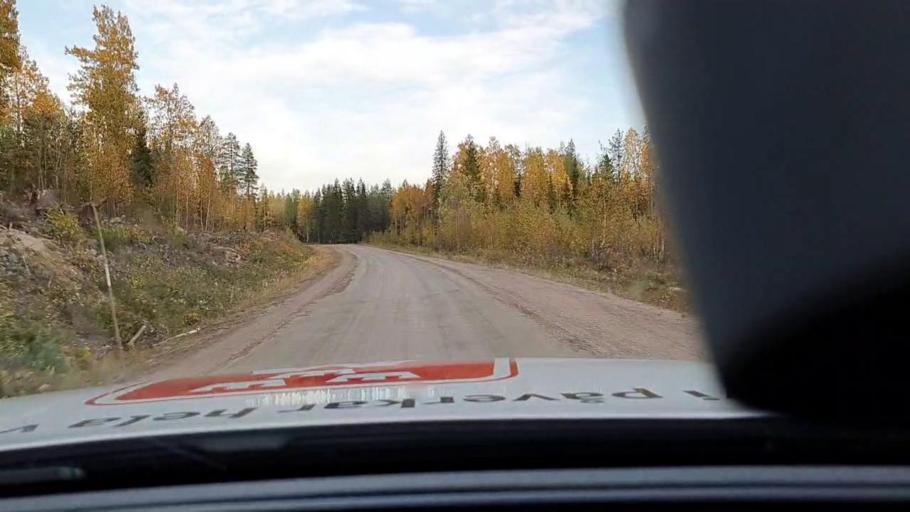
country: SE
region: Norrbotten
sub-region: Overkalix Kommun
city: OEverkalix
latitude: 66.3178
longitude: 22.6678
